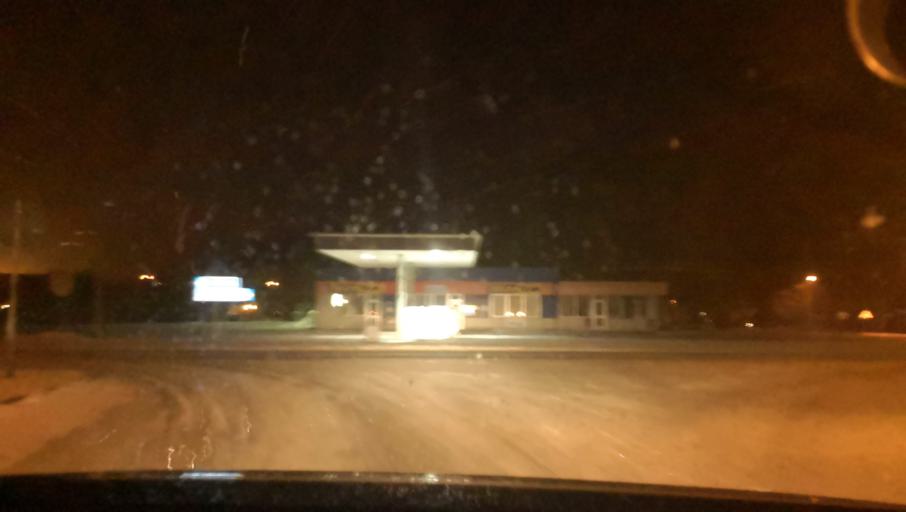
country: SE
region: Uppsala
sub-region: Heby Kommun
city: Tarnsjo
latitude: 60.1630
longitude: 16.9387
